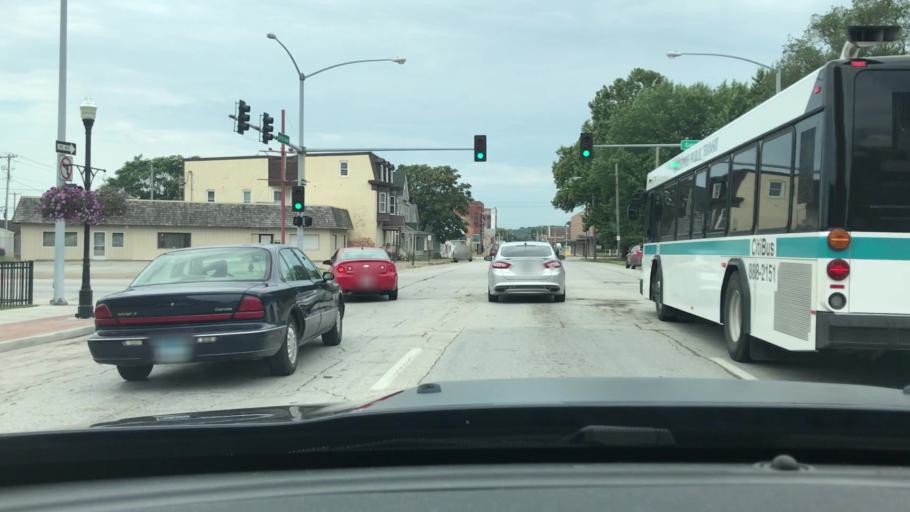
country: US
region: Iowa
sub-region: Scott County
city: Davenport
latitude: 41.5235
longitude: -90.5827
